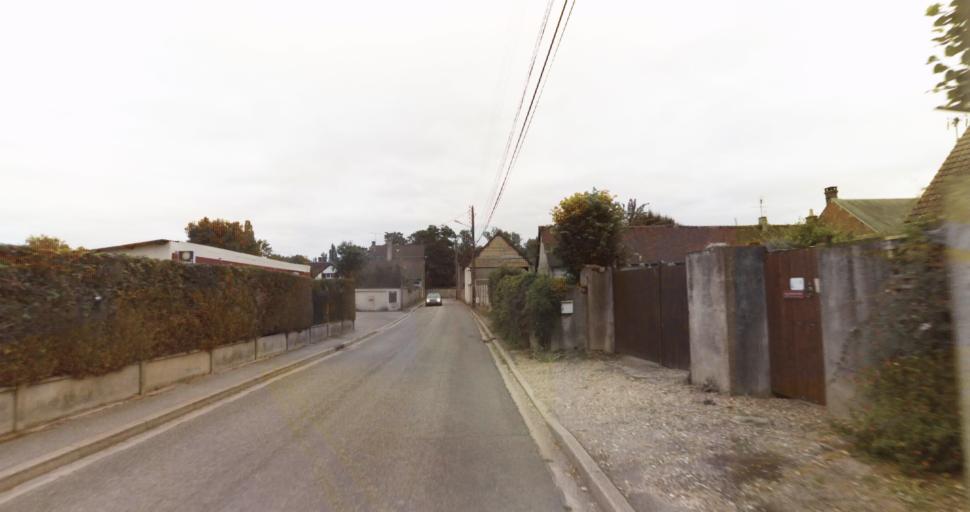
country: FR
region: Centre
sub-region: Departement d'Eure-et-Loir
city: Vert-en-Drouais
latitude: 48.7733
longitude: 1.3023
